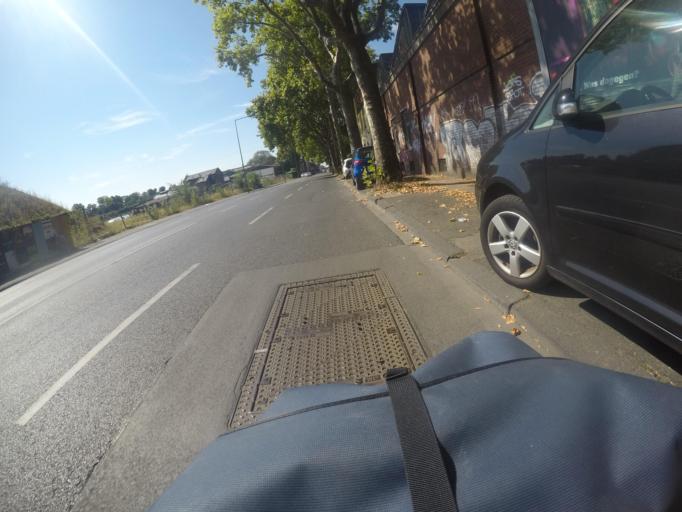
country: DE
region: North Rhine-Westphalia
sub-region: Regierungsbezirk Koln
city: Buchforst
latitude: 50.9572
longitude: 6.9940
